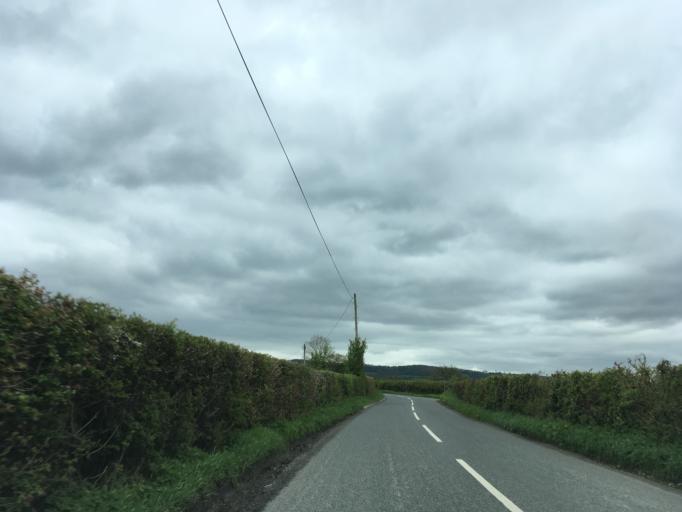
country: GB
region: England
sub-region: Gloucestershire
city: Wotton-under-Edge
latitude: 51.6177
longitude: -2.3621
